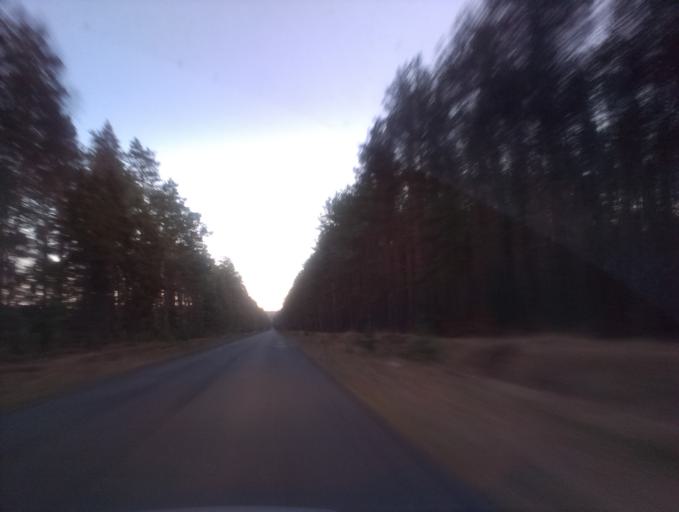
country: PL
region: Greater Poland Voivodeship
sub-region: Powiat zlotowski
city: Okonek
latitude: 53.5076
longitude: 16.9774
